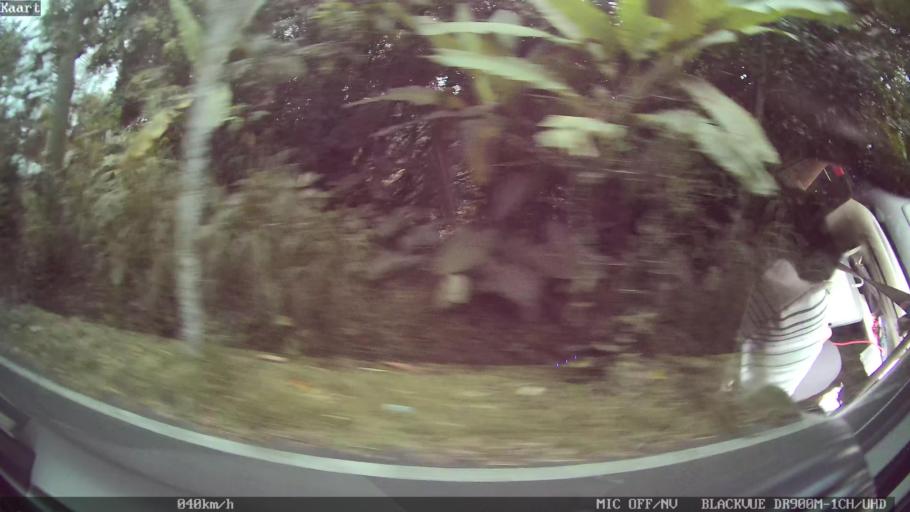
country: ID
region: Bali
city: Petang
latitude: -8.3804
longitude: 115.2225
